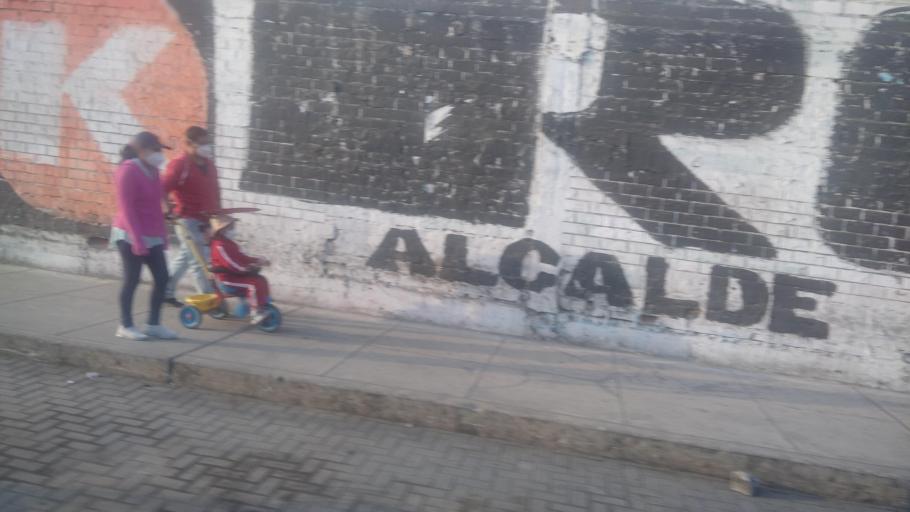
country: PE
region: Lima
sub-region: Lima
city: Vitarte
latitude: -12.0242
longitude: -76.9749
